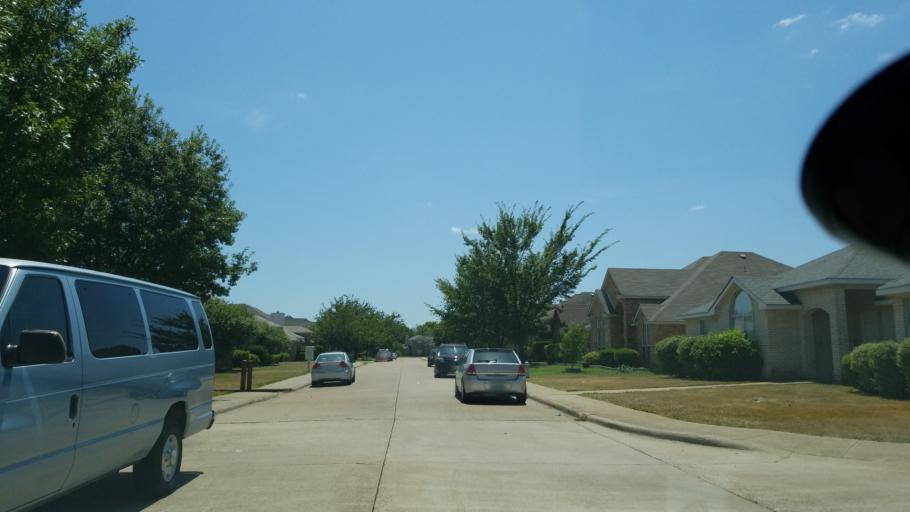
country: US
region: Texas
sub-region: Dallas County
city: Duncanville
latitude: 32.6394
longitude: -96.8841
